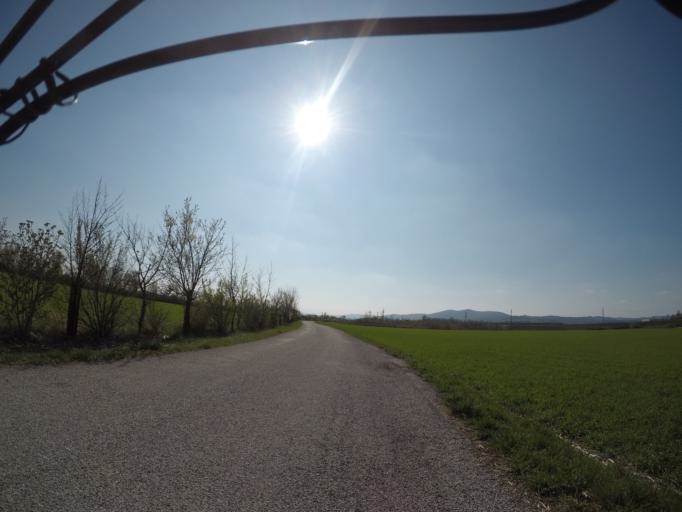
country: AT
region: Lower Austria
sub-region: Politischer Bezirk Modling
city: Laxenburg
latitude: 48.0632
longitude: 16.3479
